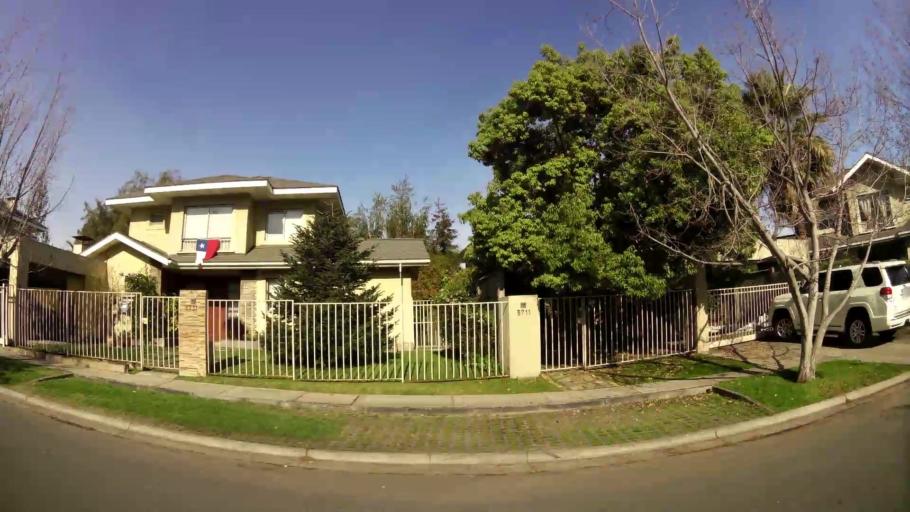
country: CL
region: Santiago Metropolitan
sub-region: Provincia de Santiago
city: Villa Presidente Frei, Nunoa, Santiago, Chile
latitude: -33.4899
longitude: -70.5534
